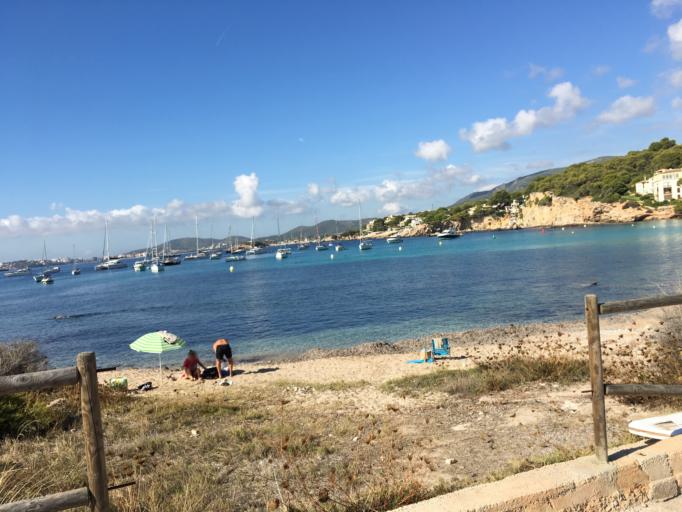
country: ES
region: Balearic Islands
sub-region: Illes Balears
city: Magaluf
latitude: 39.5321
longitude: 2.5896
